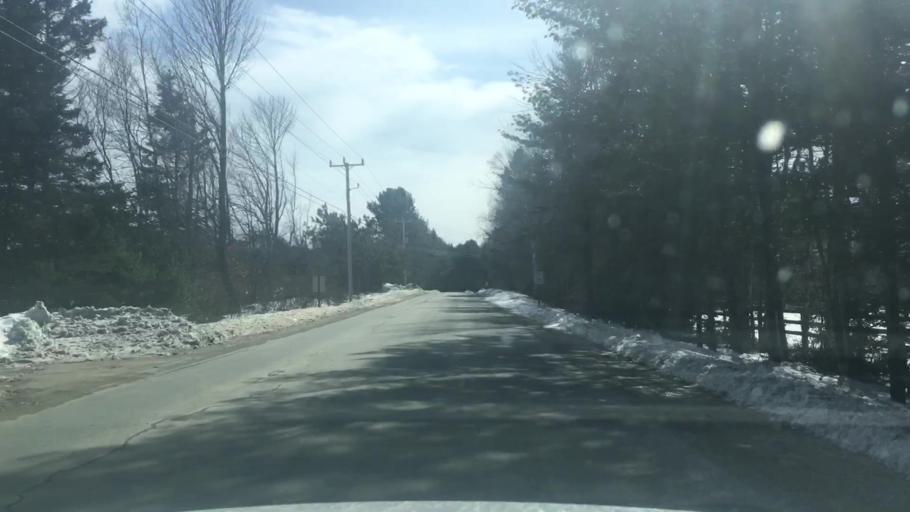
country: US
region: Maine
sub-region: Penobscot County
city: Holden
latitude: 44.7686
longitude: -68.6480
